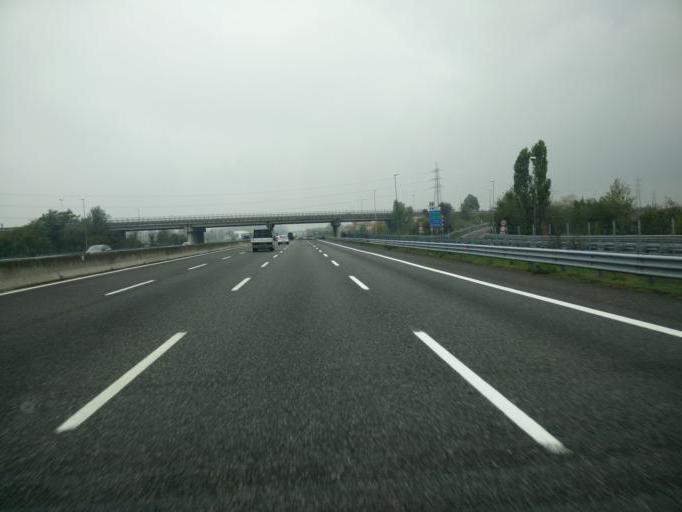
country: IT
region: Emilia-Romagna
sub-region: Provincia di Modena
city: Baggiovara
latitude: 44.6268
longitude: 10.8796
